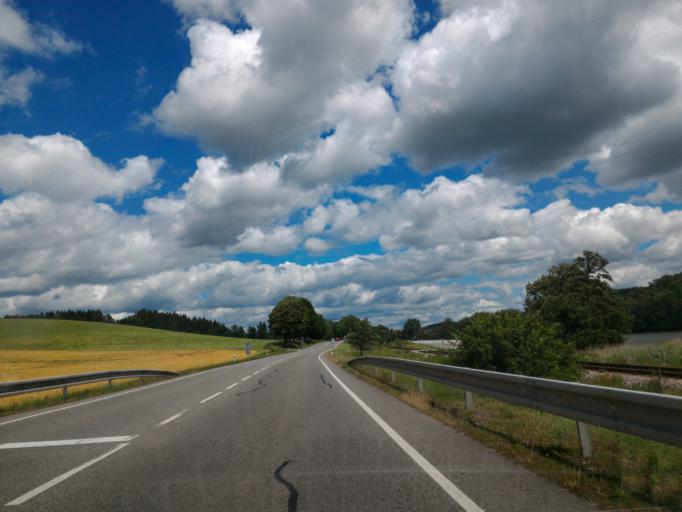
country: CZ
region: Vysocina
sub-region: Okres Jihlava
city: Trest'
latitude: 49.3102
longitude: 15.4802
